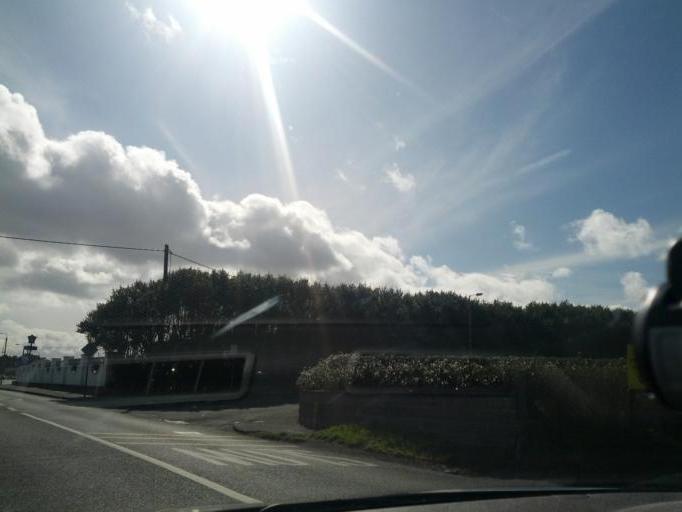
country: IE
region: Leinster
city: Portmarnock
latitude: 53.4361
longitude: -6.1226
